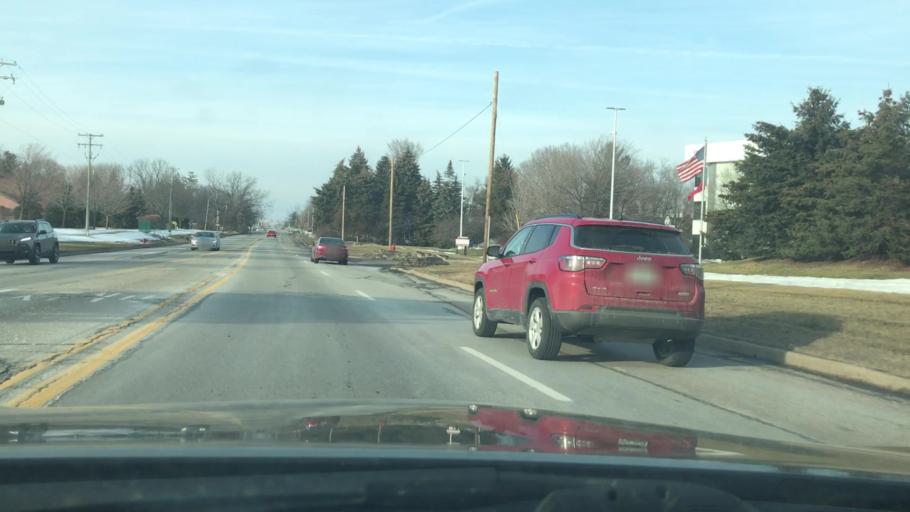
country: US
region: Michigan
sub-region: Oakland County
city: Novi
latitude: 42.4492
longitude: -83.4341
